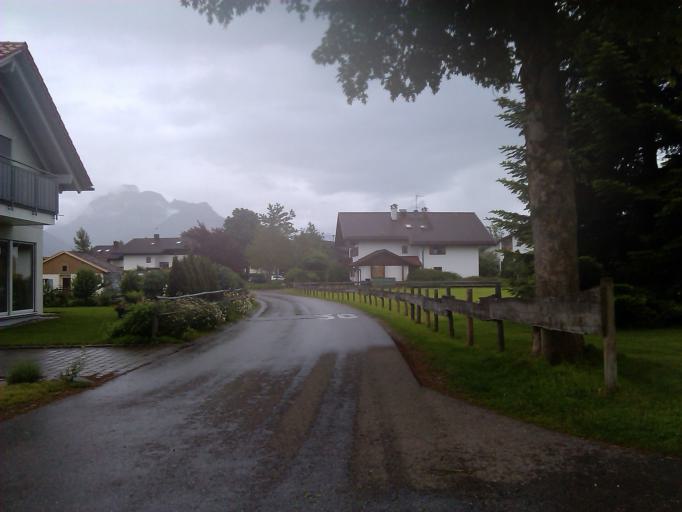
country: DE
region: Bavaria
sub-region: Swabia
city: Rosshaupten
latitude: 47.6162
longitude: 10.7229
